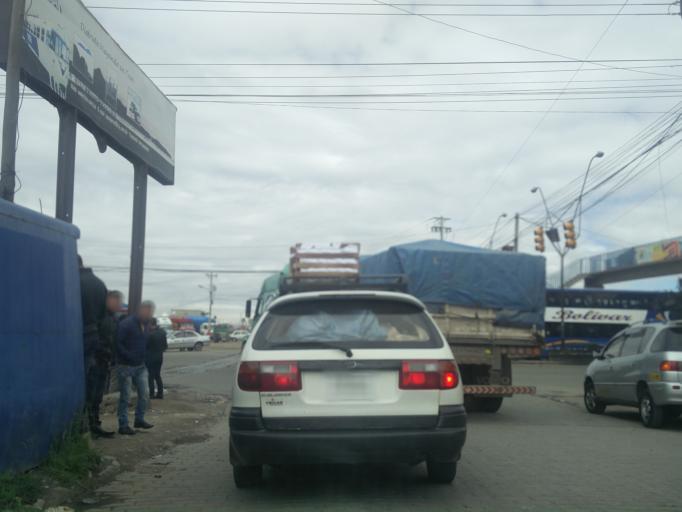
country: BO
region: La Paz
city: La Paz
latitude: -16.5235
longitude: -68.1689
